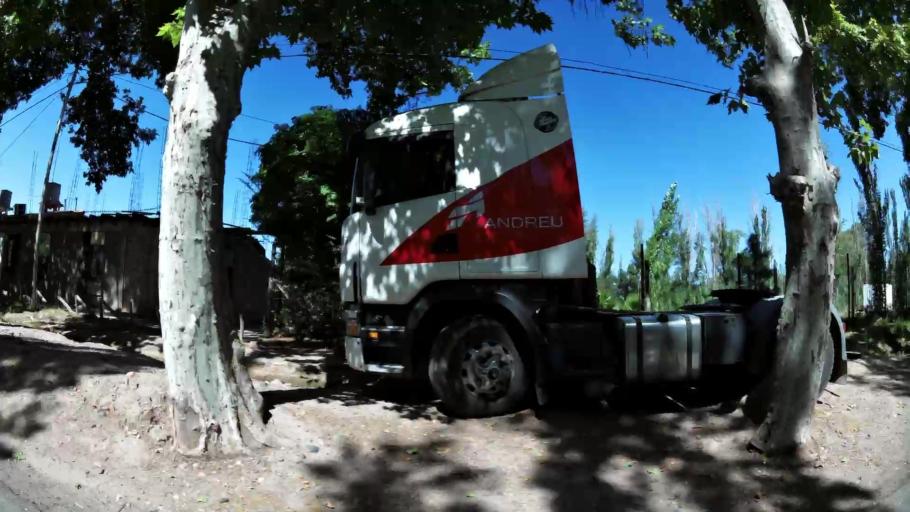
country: AR
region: Mendoza
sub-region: Departamento de Godoy Cruz
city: Godoy Cruz
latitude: -32.9753
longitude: -68.8395
